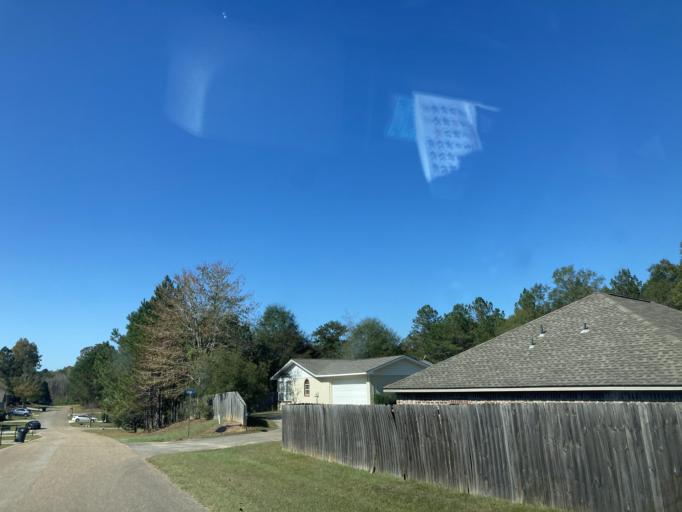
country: US
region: Mississippi
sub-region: Lamar County
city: West Hattiesburg
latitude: 31.3081
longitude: -89.4938
